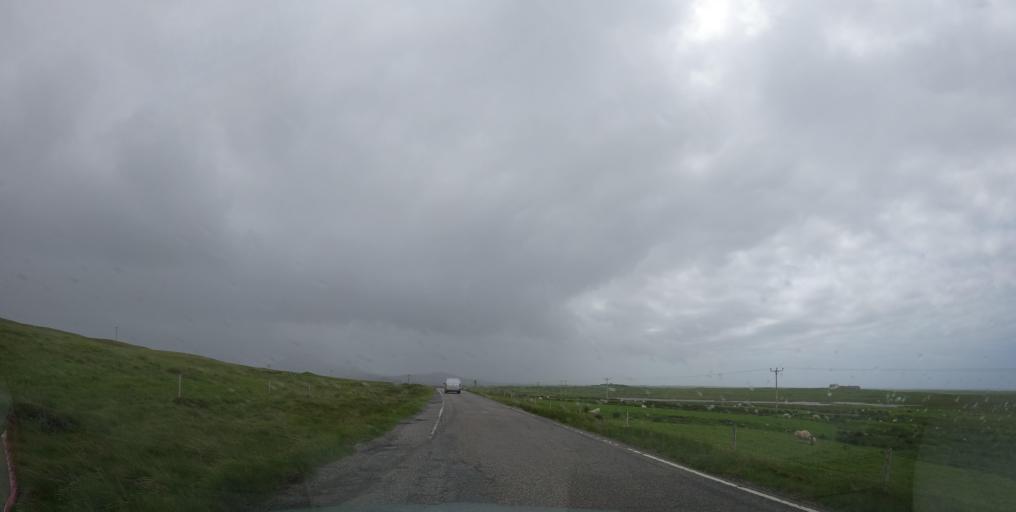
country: GB
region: Scotland
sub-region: Eilean Siar
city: Isle of South Uist
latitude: 57.3427
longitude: -7.3648
